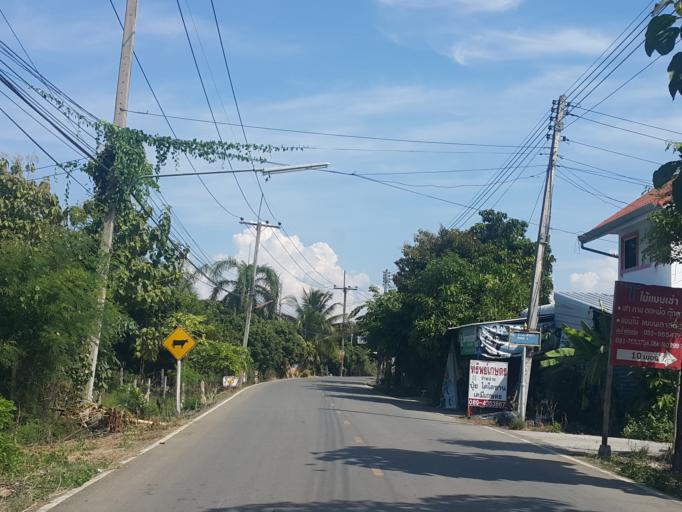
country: TH
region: Chiang Mai
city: San Kamphaeng
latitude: 18.7931
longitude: 99.1309
